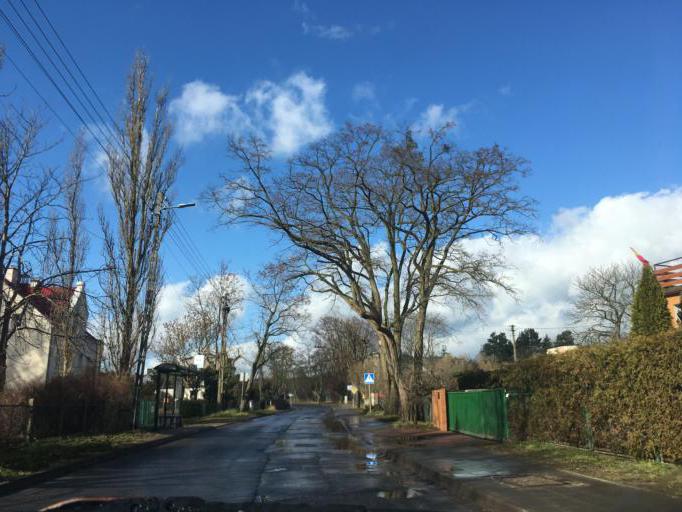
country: PL
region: Pomeranian Voivodeship
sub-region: Powiat gdanski
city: Cedry Wielkie
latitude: 54.3458
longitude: 18.8208
